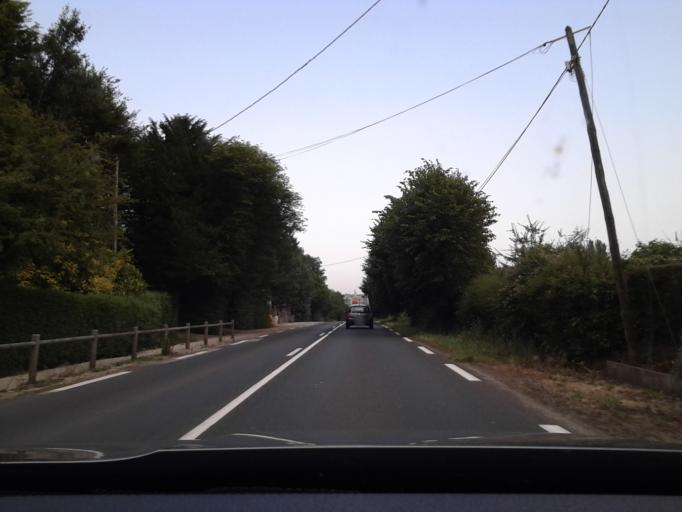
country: FR
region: Lower Normandy
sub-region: Departement de la Manche
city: Valognes
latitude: 49.5164
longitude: -1.4887
